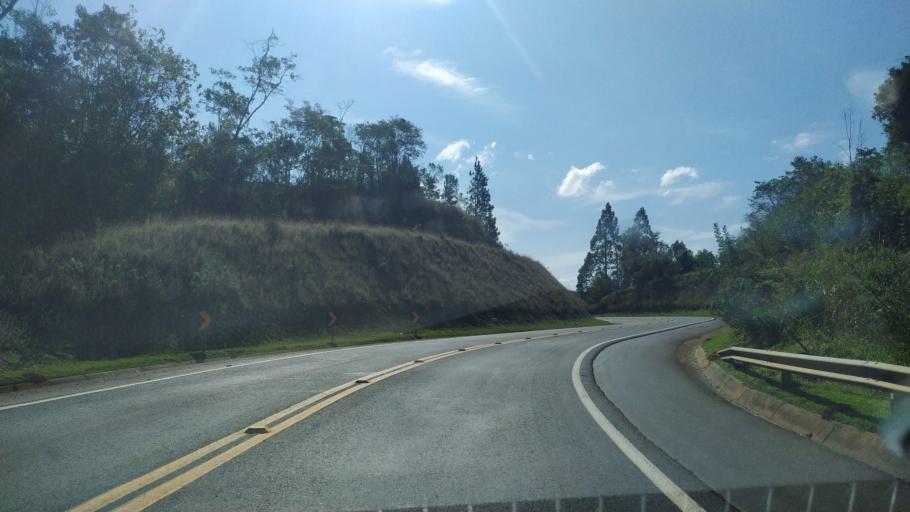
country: BR
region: Parana
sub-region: Telemaco Borba
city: Telemaco Borba
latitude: -24.2734
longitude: -50.7163
